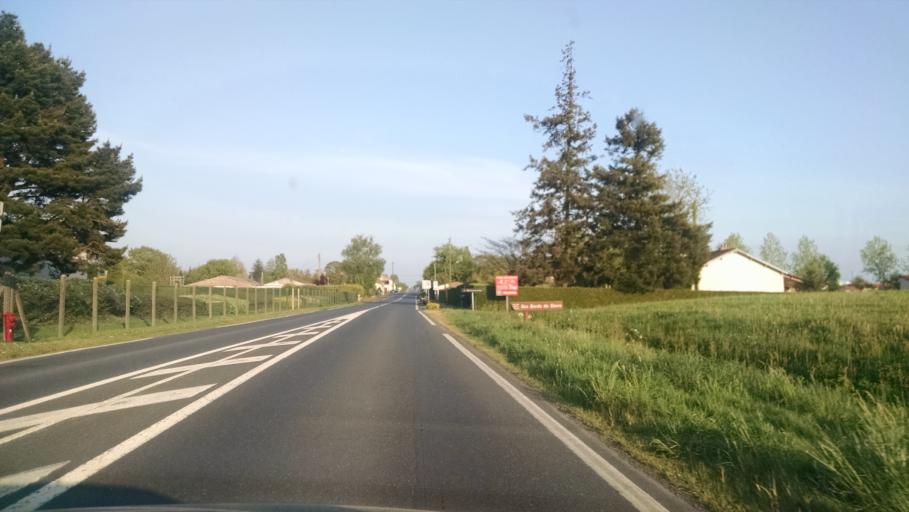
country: FR
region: Pays de la Loire
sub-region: Departement de la Loire-Atlantique
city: Boussay
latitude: 47.0598
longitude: -1.1849
